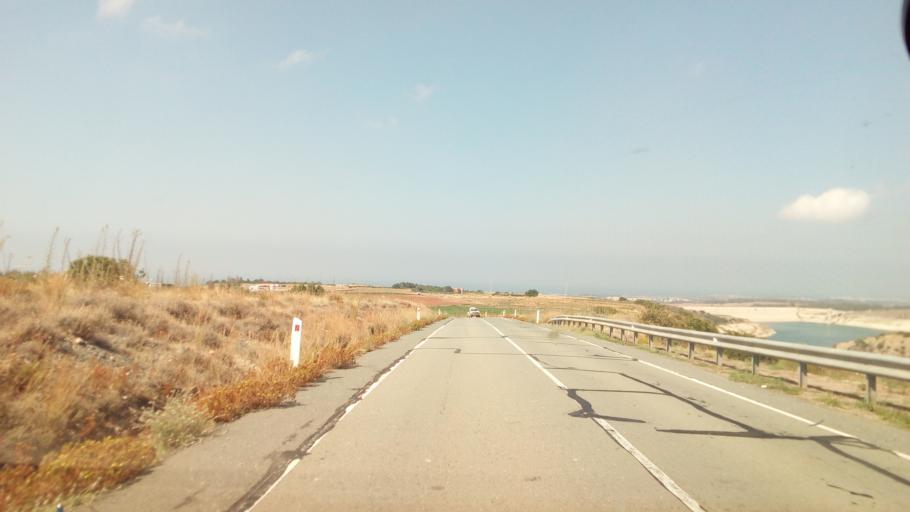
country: CY
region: Limassol
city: Pissouri
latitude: 34.7313
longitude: 32.5727
